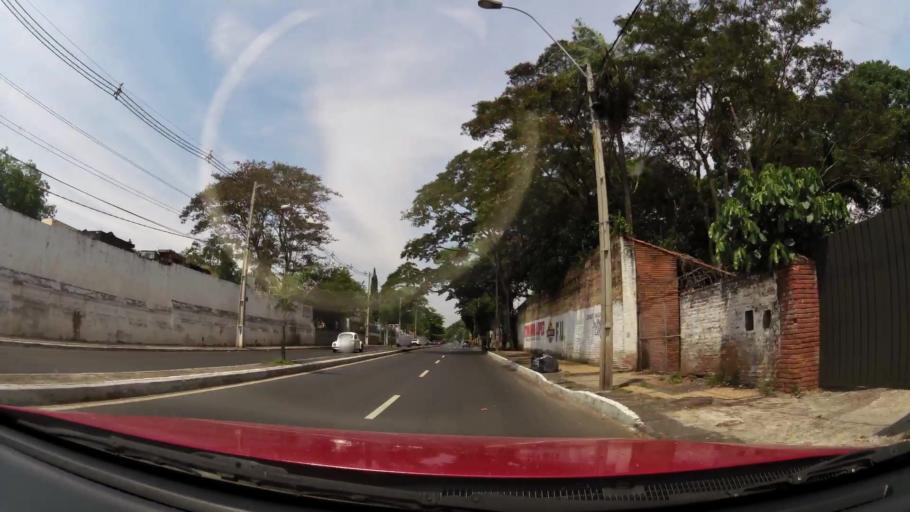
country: PY
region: Asuncion
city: Asuncion
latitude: -25.2918
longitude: -57.5915
